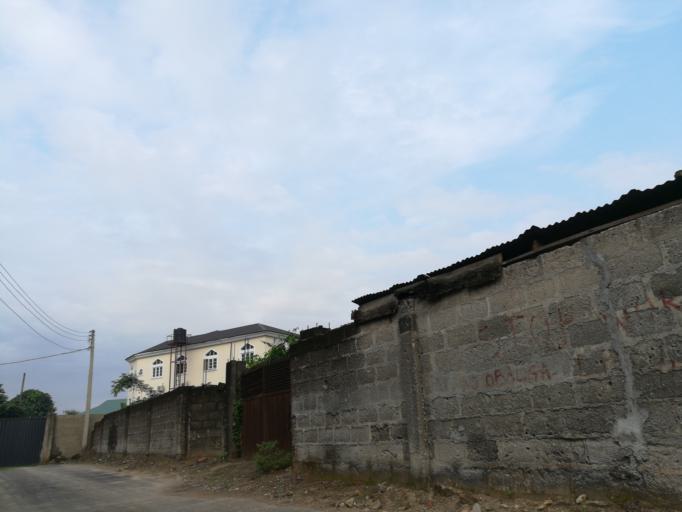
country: NG
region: Rivers
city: Port Harcourt
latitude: 4.8436
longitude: 7.0534
